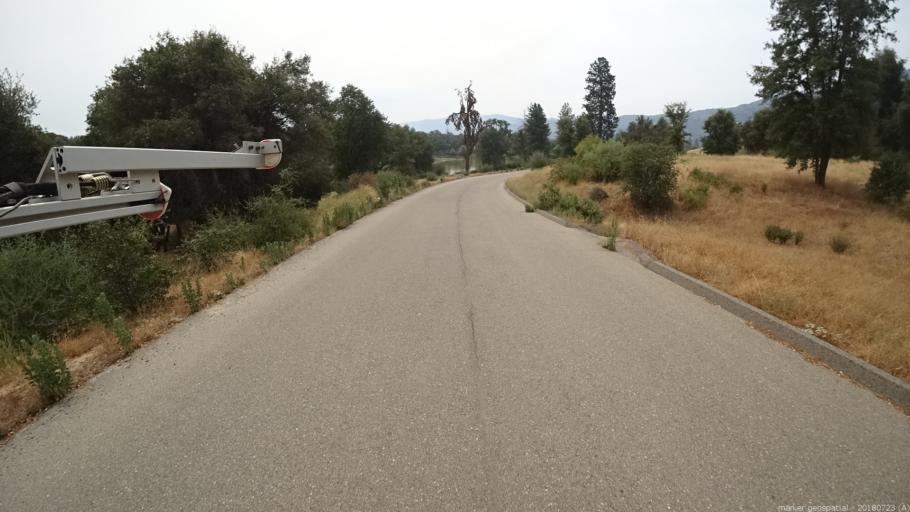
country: US
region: California
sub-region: Madera County
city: Oakhurst
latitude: 37.3440
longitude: -119.6677
